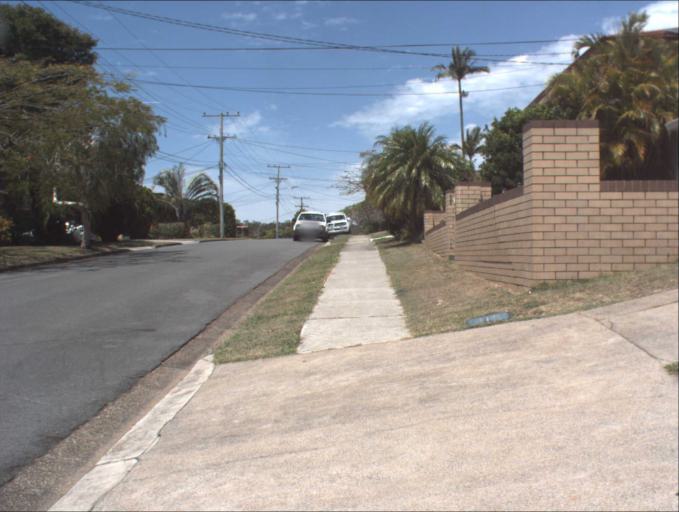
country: AU
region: Queensland
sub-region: Logan
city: Rochedale South
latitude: -27.5950
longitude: 153.1421
